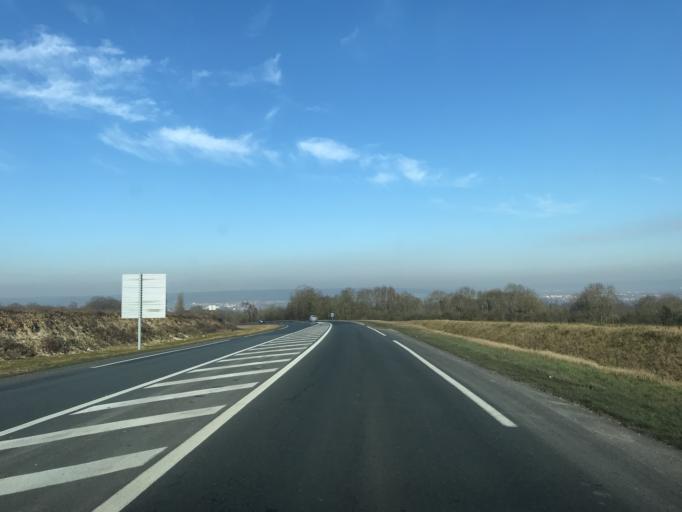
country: FR
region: Haute-Normandie
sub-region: Departement de l'Eure
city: Saint-Pierre-du-Vauvray
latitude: 49.2281
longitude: 1.2116
